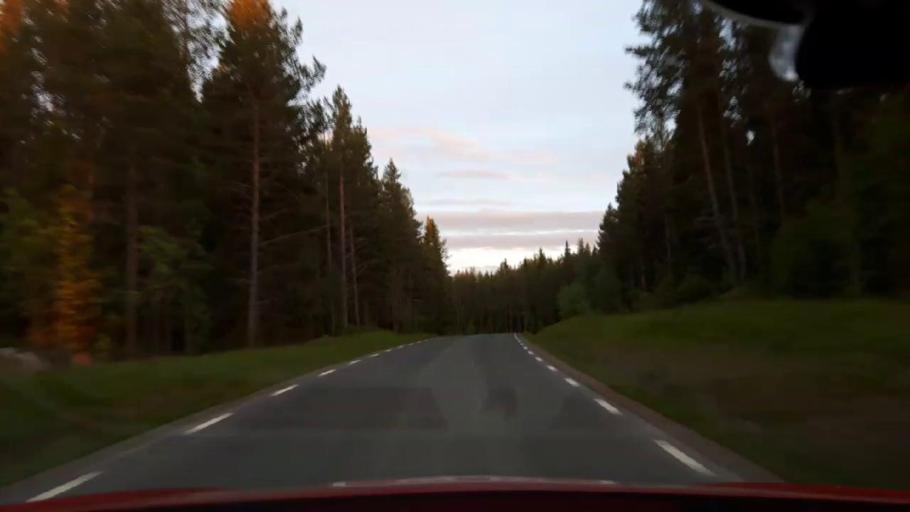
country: SE
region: Jaemtland
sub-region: OEstersunds Kommun
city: Brunflo
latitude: 63.0639
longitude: 14.8034
